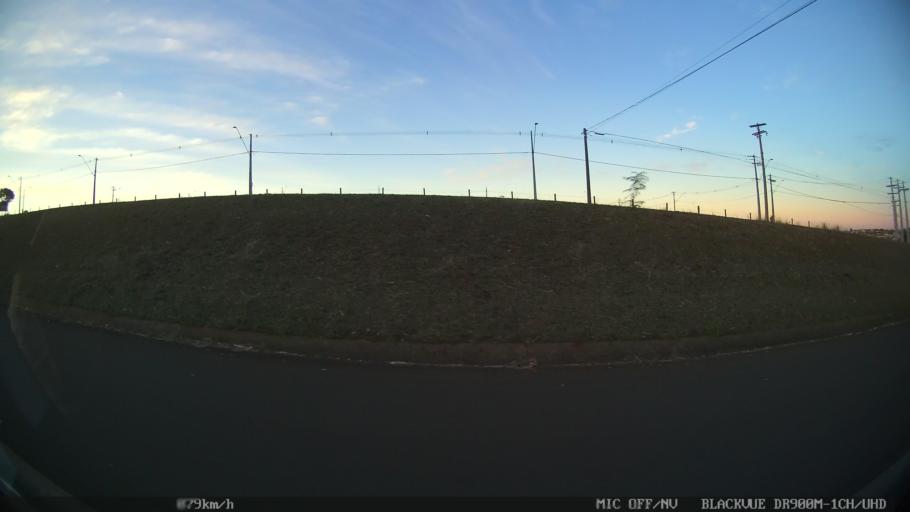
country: BR
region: Sao Paulo
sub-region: Catanduva
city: Catanduva
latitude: -21.1418
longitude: -49.0099
